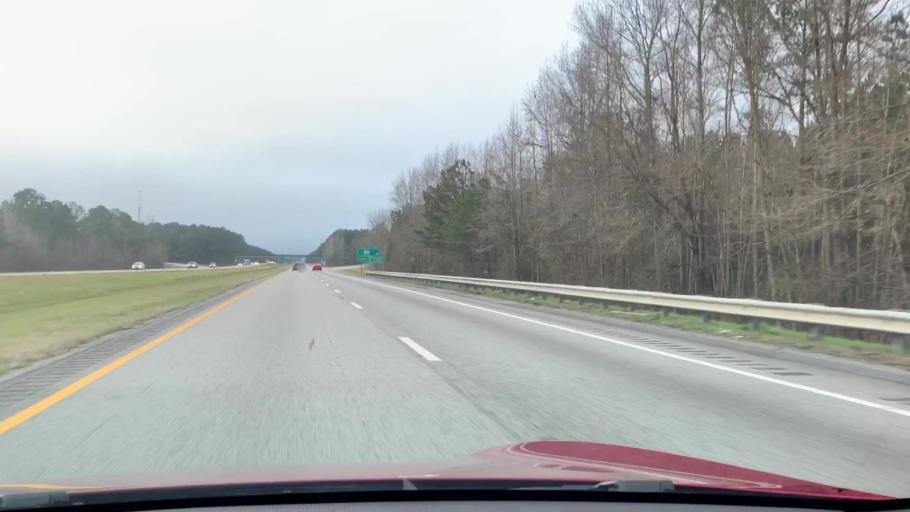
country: US
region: South Carolina
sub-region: Florence County
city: Timmonsville
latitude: 34.0298
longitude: -79.9913
